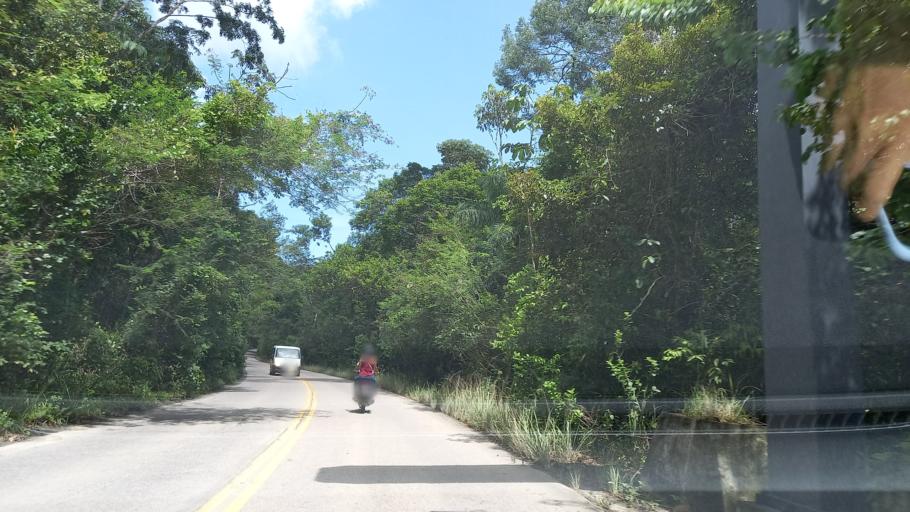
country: BR
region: Pernambuco
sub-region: Rio Formoso
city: Rio Formoso
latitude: -8.7341
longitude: -35.1737
